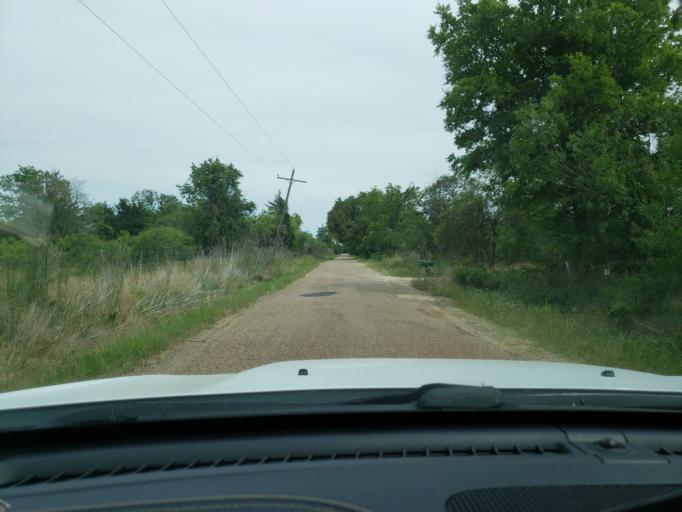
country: US
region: Texas
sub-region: Burleson County
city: Somerville
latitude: 30.3530
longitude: -96.5453
